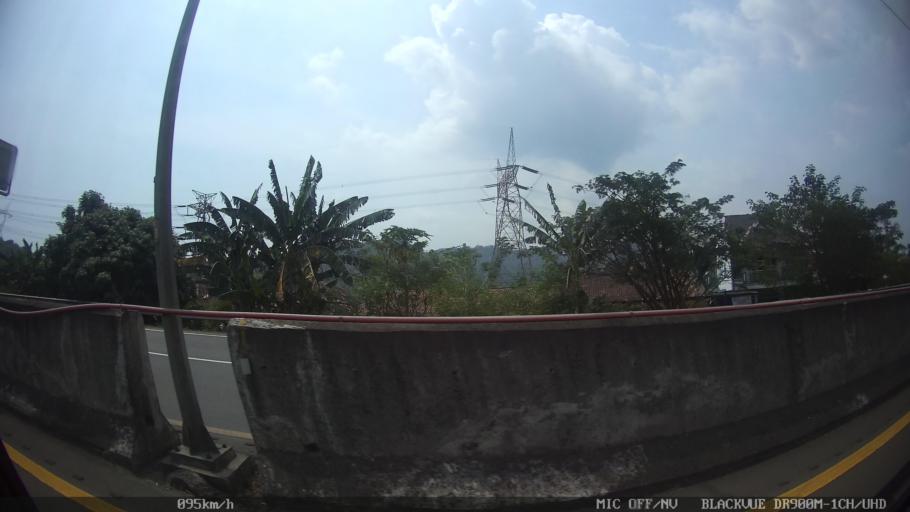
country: ID
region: Banten
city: Curug
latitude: -5.9820
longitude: 106.0284
